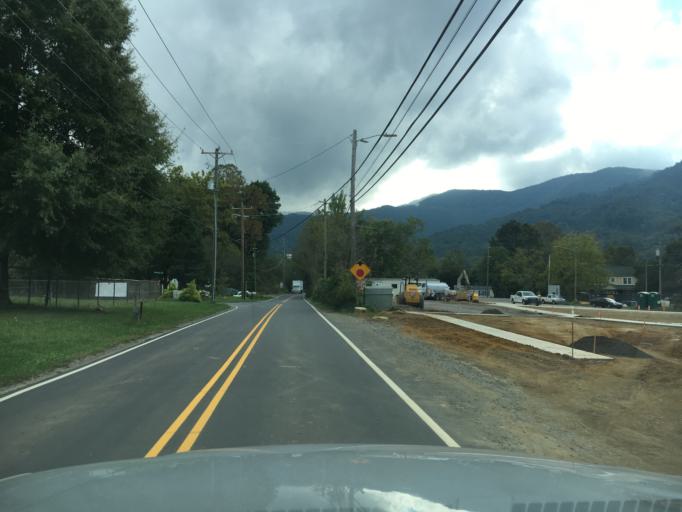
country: US
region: North Carolina
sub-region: Buncombe County
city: Swannanoa
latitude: 35.6035
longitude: -82.4037
